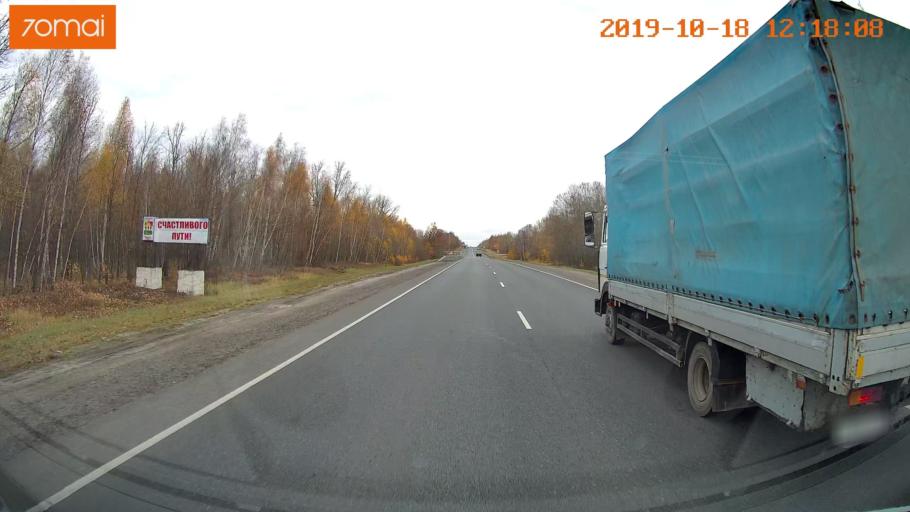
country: RU
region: Rjazan
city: Zakharovo
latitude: 54.4637
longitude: 39.4530
